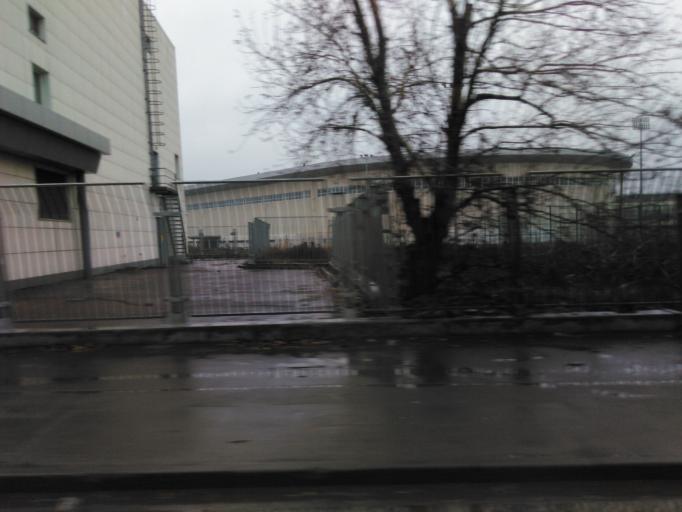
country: RU
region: Tatarstan
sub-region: Gorod Kazan'
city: Kazan
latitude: 55.7952
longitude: 49.0940
